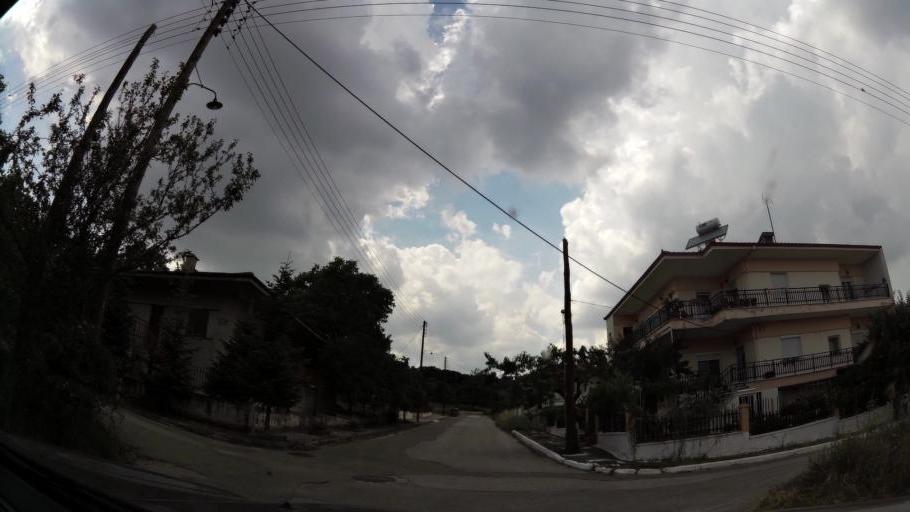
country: GR
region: West Macedonia
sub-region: Nomos Kozanis
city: Koila
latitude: 40.3272
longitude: 21.8210
